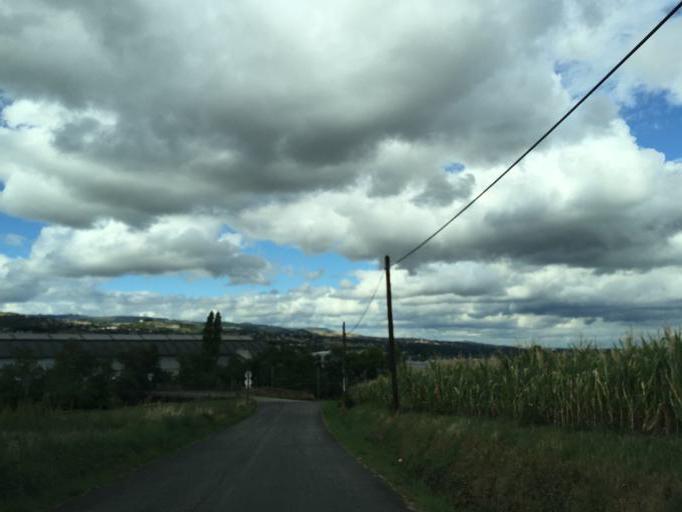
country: FR
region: Rhone-Alpes
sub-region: Departement de la Loire
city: La Grand-Croix
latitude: 45.4837
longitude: 4.5496
